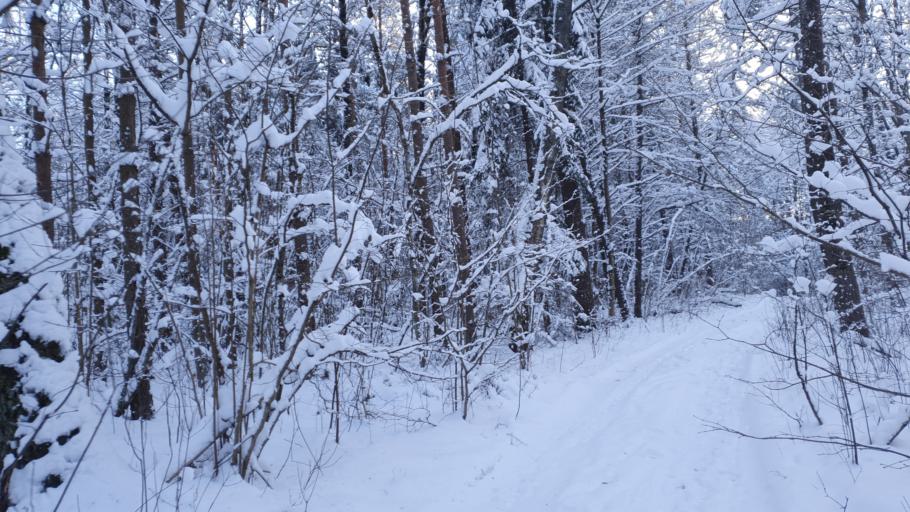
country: LT
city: Skaidiskes
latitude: 54.6438
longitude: 25.4173
